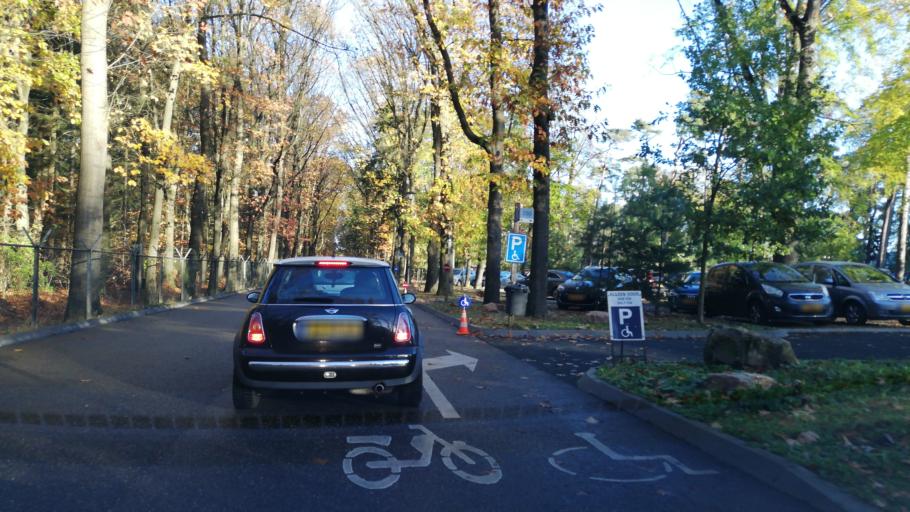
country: NL
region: Gelderland
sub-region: Gemeente Arnhem
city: Gulden Bodem
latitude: 52.0075
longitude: 5.8967
